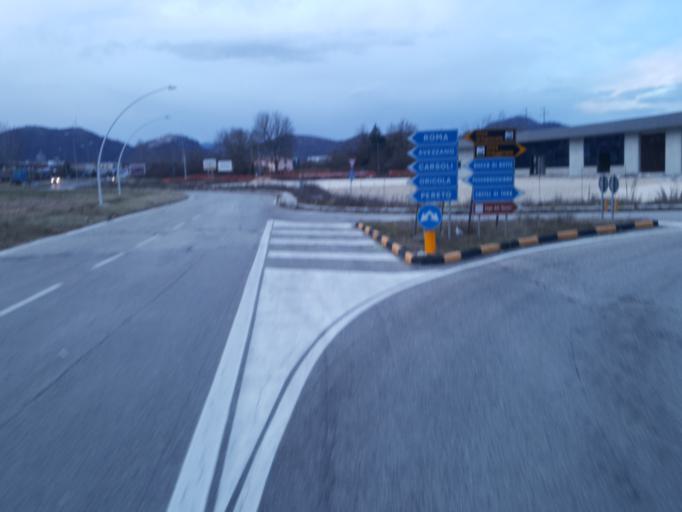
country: IT
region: Abruzzo
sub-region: Provincia dell' Aquila
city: Carsoli
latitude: 42.0807
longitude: 13.0577
